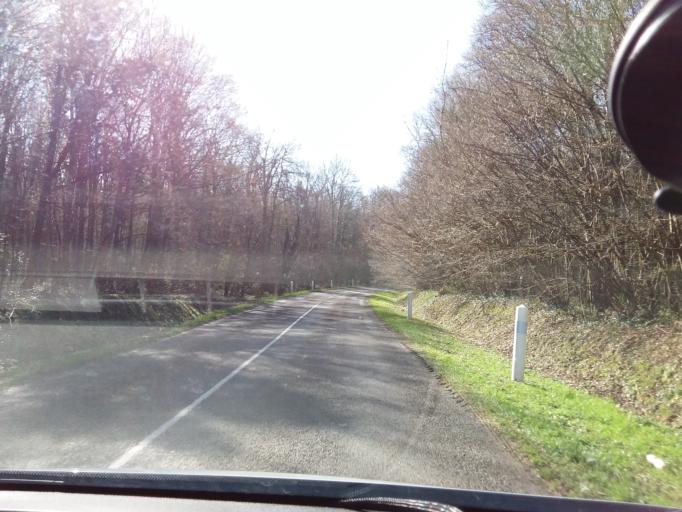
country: FR
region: Picardie
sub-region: Departement de l'Aisne
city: Hirson
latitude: 49.9511
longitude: 4.0782
